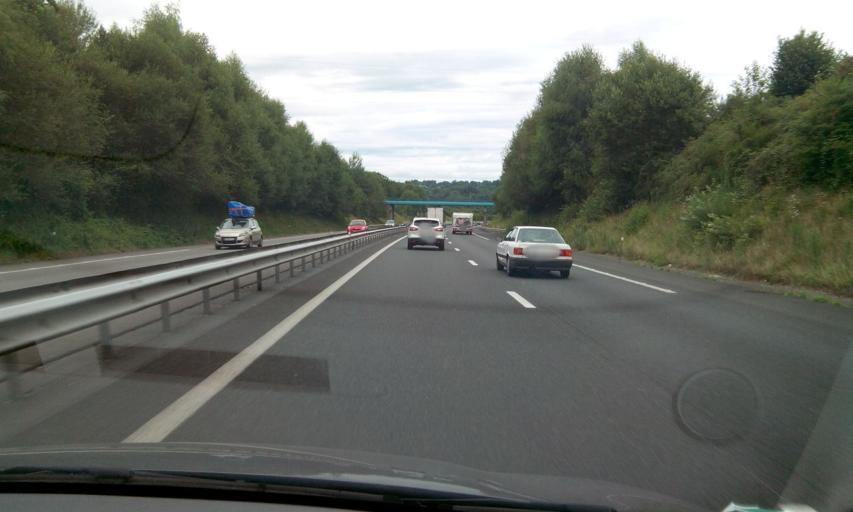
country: FR
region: Limousin
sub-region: Departement de la Correze
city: Uzerche
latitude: 45.4070
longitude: 1.5406
